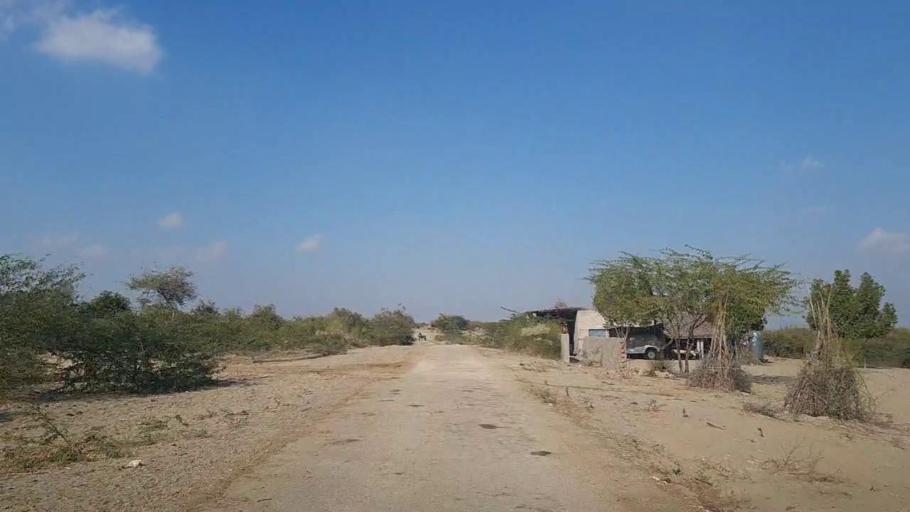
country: PK
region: Sindh
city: Tando Mittha Khan
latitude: 26.0195
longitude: 69.2506
